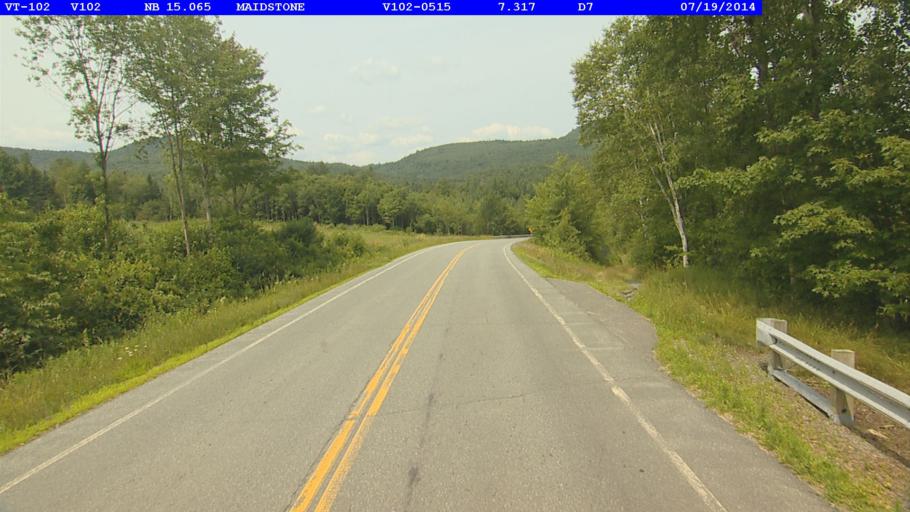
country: US
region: New Hampshire
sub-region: Coos County
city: Stratford
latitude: 44.6558
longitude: -71.5892
